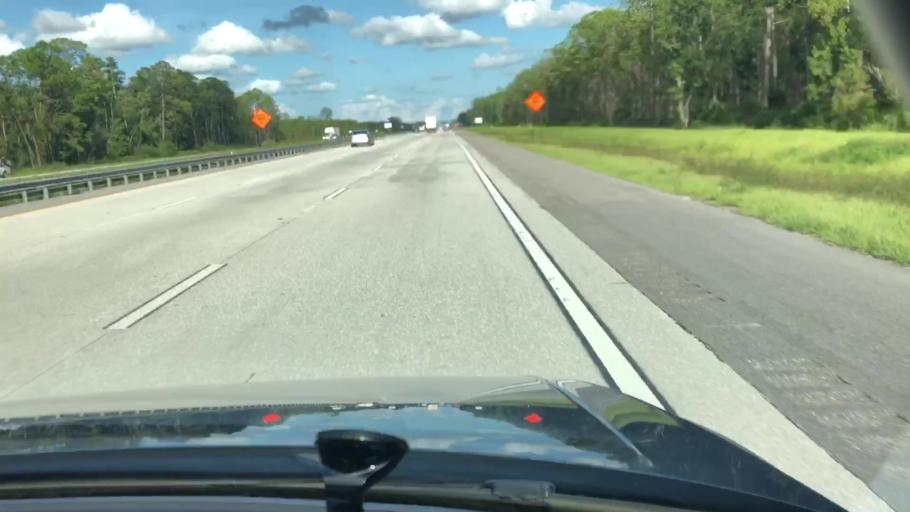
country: US
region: Florida
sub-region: Volusia County
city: Samsula-Spruce Creek
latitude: 29.1399
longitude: -81.1117
